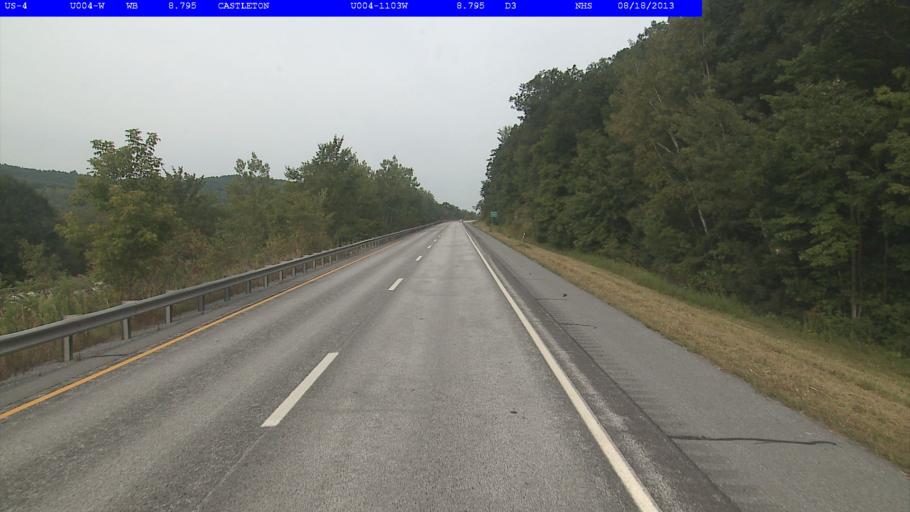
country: US
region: Vermont
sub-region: Rutland County
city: Castleton
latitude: 43.6153
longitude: -73.1441
